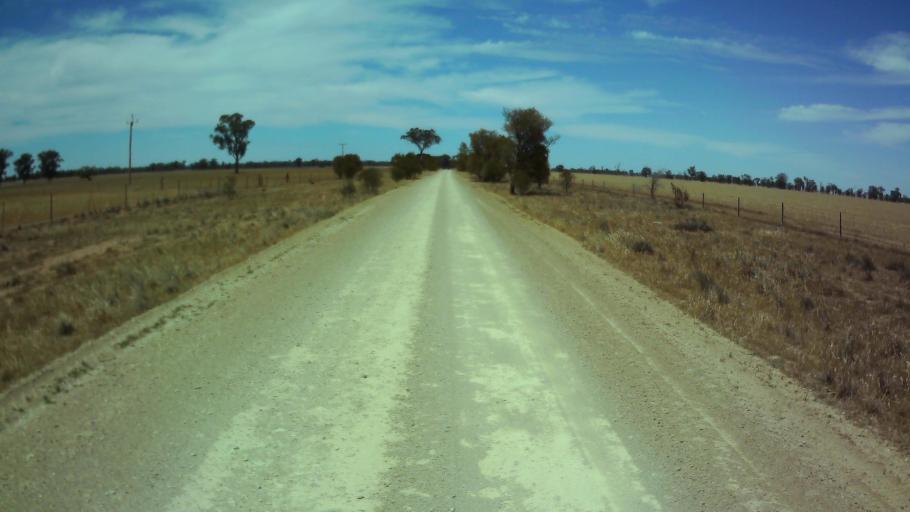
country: AU
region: New South Wales
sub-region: Weddin
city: Grenfell
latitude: -33.8779
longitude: 147.8051
